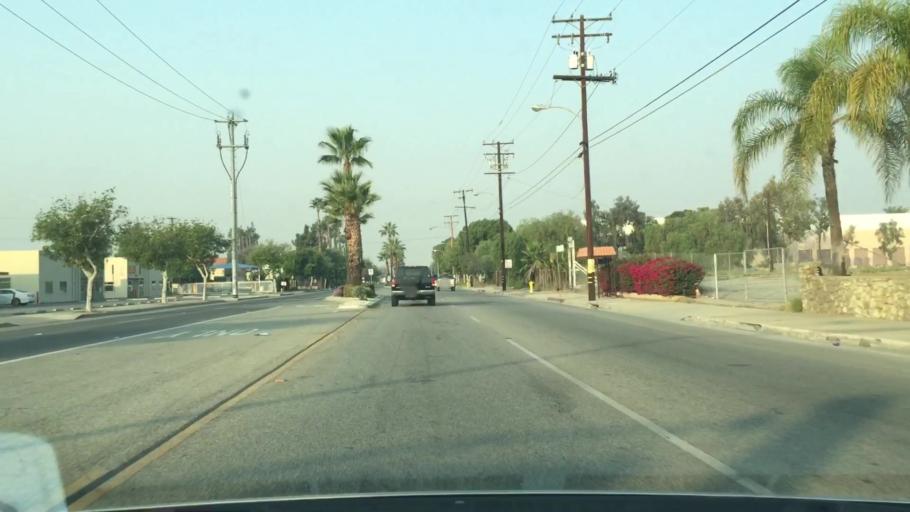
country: US
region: California
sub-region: Los Angeles County
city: Irwindale
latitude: 34.1070
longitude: -117.9283
